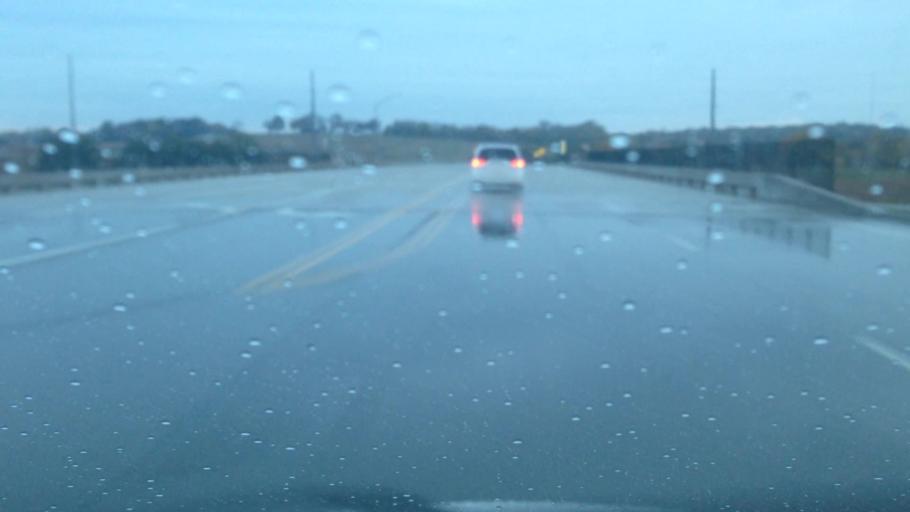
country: US
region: Kansas
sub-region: Douglas County
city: Lawrence
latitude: 38.9610
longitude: -95.3340
